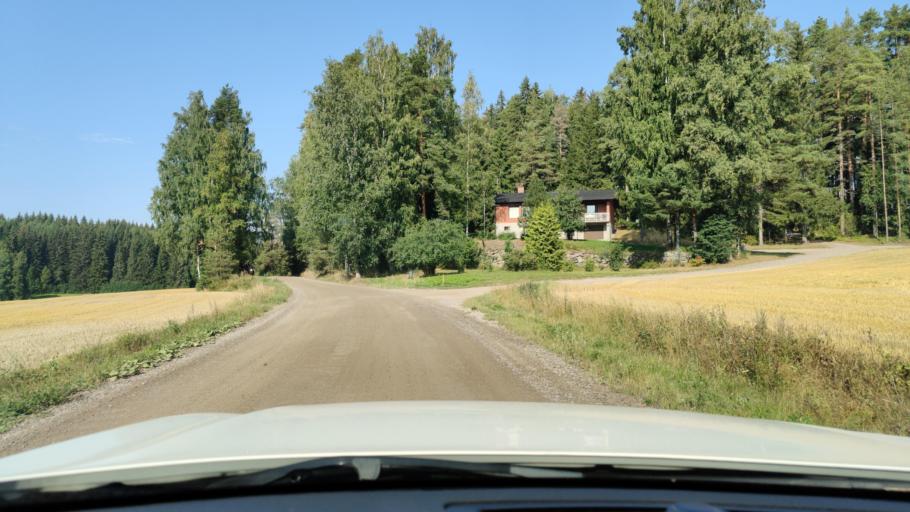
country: FI
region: Haeme
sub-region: Haemeenlinna
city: Tervakoski
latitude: 60.6747
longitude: 24.6032
